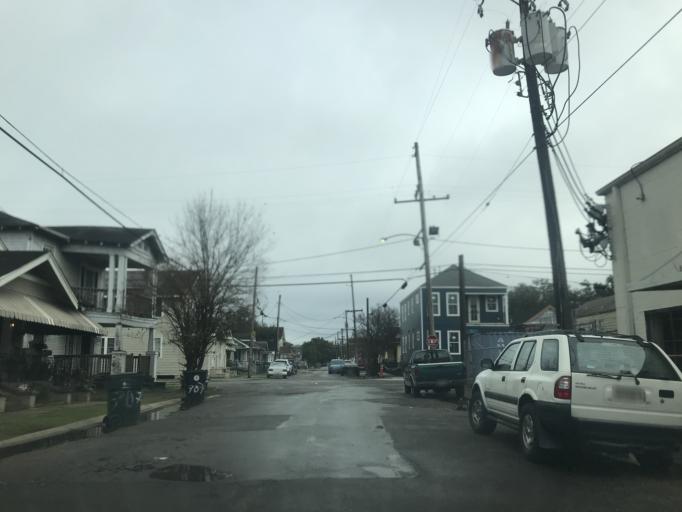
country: US
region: Louisiana
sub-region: Orleans Parish
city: New Orleans
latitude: 29.9703
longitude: -90.1069
